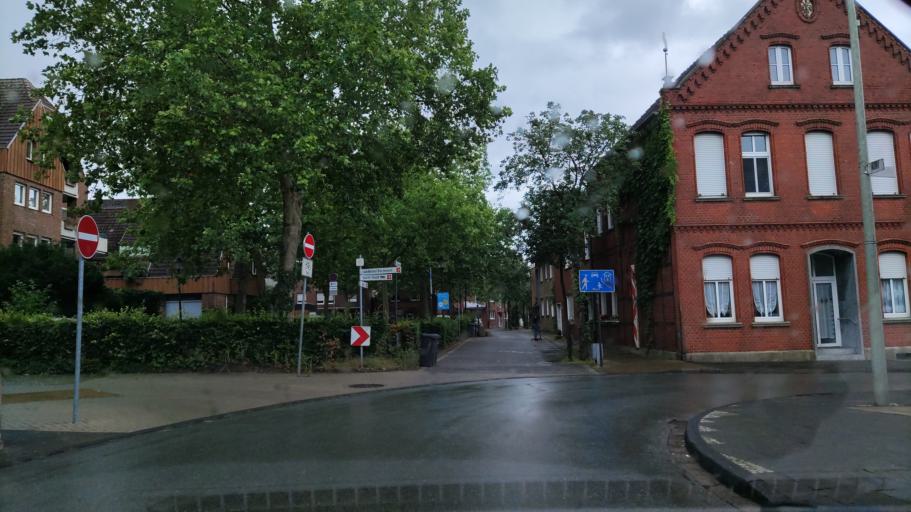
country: DE
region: North Rhine-Westphalia
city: Sendenhorst
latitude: 51.8434
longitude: 7.8276
